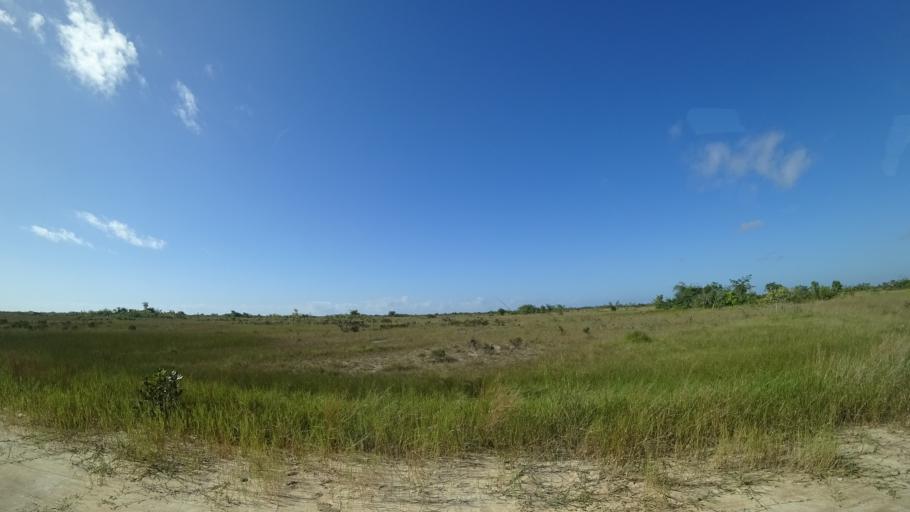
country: MZ
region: Sofala
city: Beira
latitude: -19.7002
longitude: 35.0272
